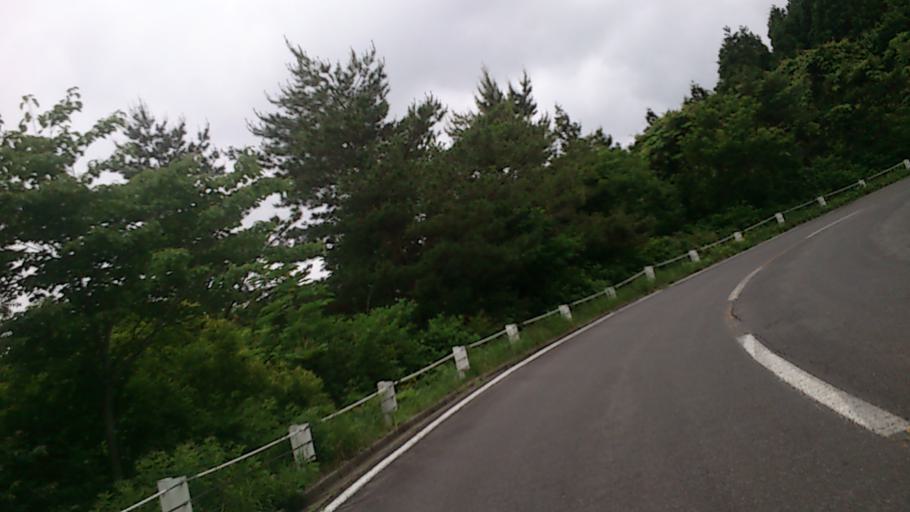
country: JP
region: Yamagata
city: Yuza
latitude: 39.1444
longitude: 139.9678
